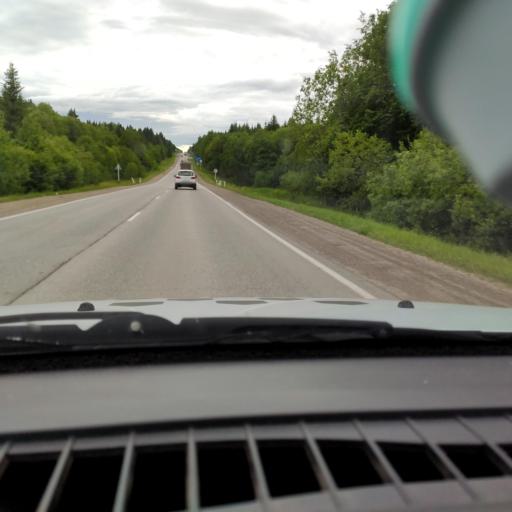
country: RU
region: Perm
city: Lys'va
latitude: 58.1169
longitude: 57.7078
